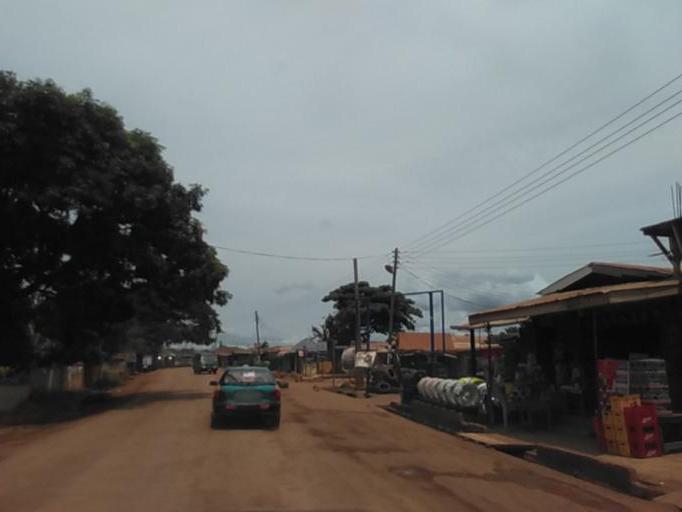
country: GH
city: Akropong
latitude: 6.1334
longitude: 0.0027
